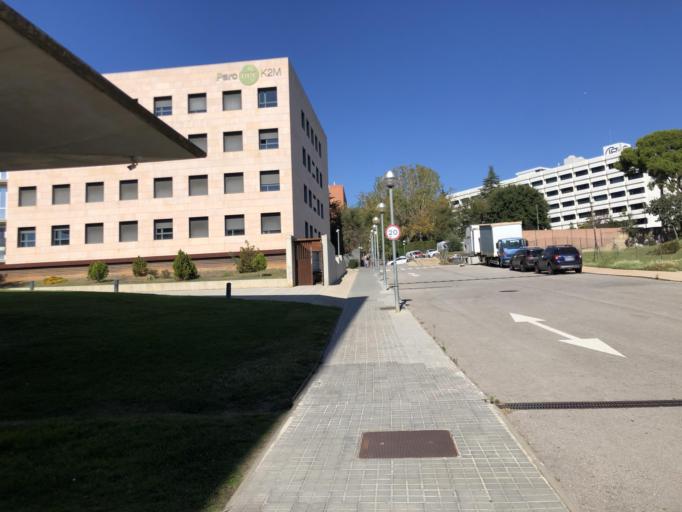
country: ES
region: Catalonia
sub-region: Provincia de Barcelona
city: les Corts
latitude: 41.3886
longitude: 2.1148
